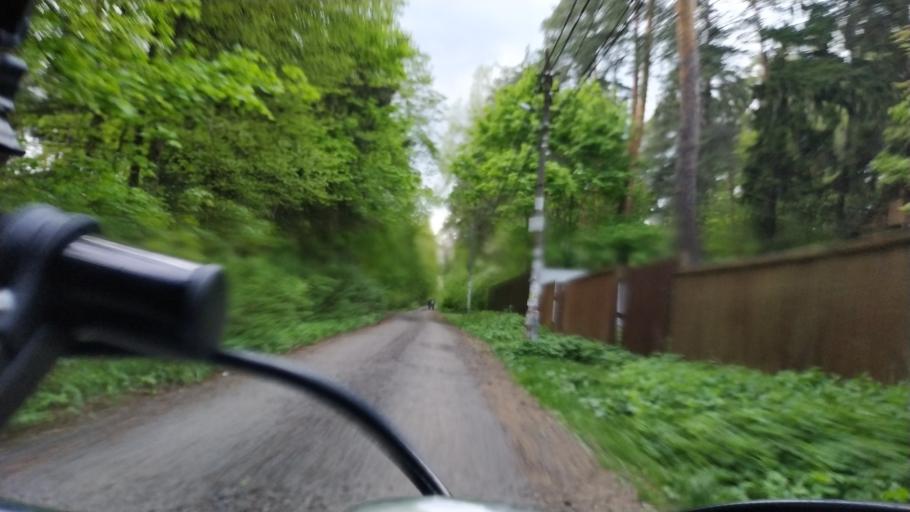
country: RU
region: Moskovskaya
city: Kratovo
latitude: 55.5813
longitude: 38.1783
